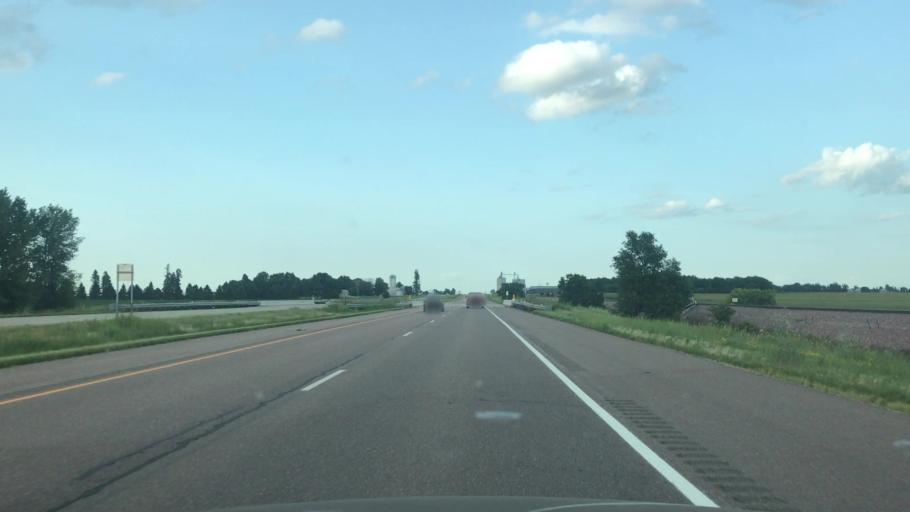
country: US
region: Minnesota
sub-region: Nobles County
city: Worthington
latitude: 43.6844
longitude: -95.4933
